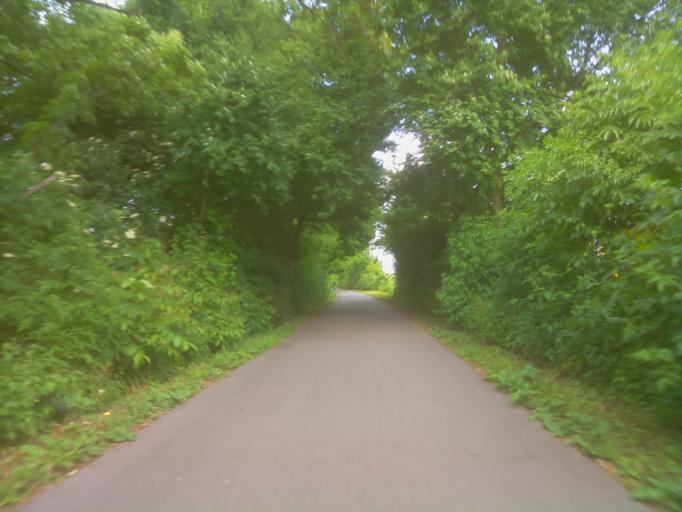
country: DE
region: Baden-Wuerttemberg
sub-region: Karlsruhe Region
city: Ilvesheim
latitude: 49.4753
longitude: 8.5335
